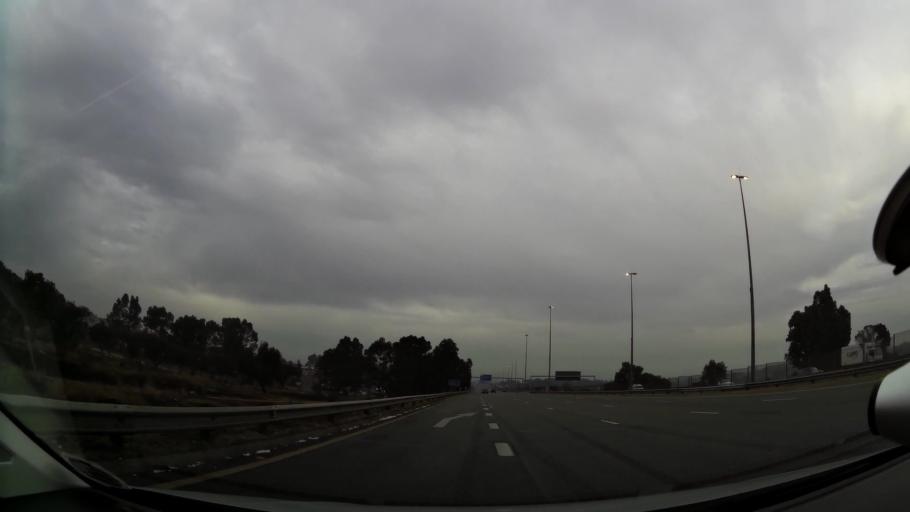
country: ZA
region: Gauteng
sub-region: City of Johannesburg Metropolitan Municipality
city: Soweto
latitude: -26.2837
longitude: 27.9470
